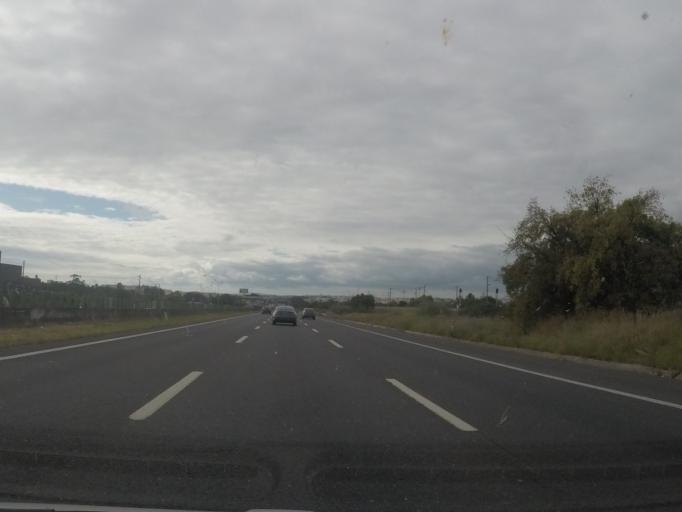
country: PT
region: Setubal
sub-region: Seixal
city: Amora
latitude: 38.6208
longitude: -9.1299
